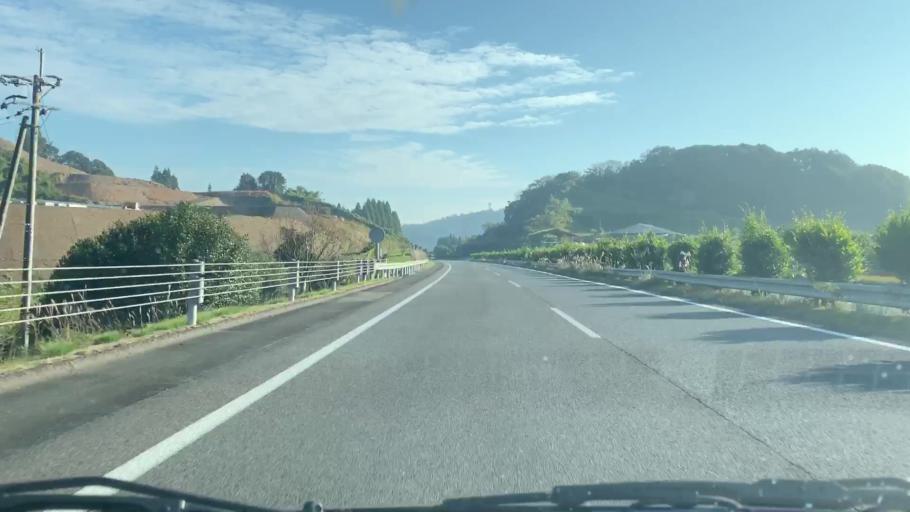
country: JP
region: Saga Prefecture
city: Takeocho-takeo
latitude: 33.2722
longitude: 130.1055
